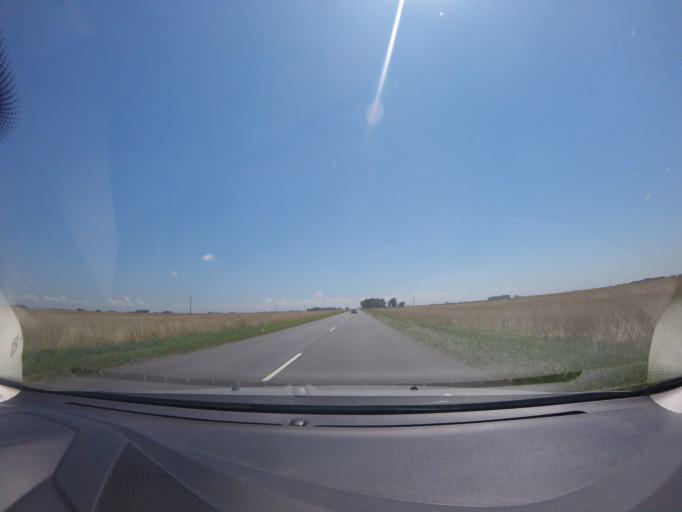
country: AR
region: Buenos Aires
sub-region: Partido de Rauch
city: Rauch
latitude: -36.5544
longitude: -59.0490
